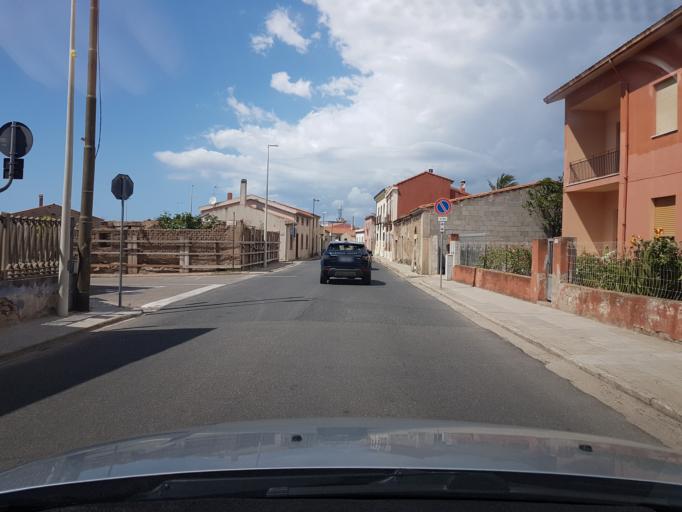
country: IT
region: Sardinia
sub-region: Provincia di Oristano
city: Riola Sardo
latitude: 39.9932
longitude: 8.5414
